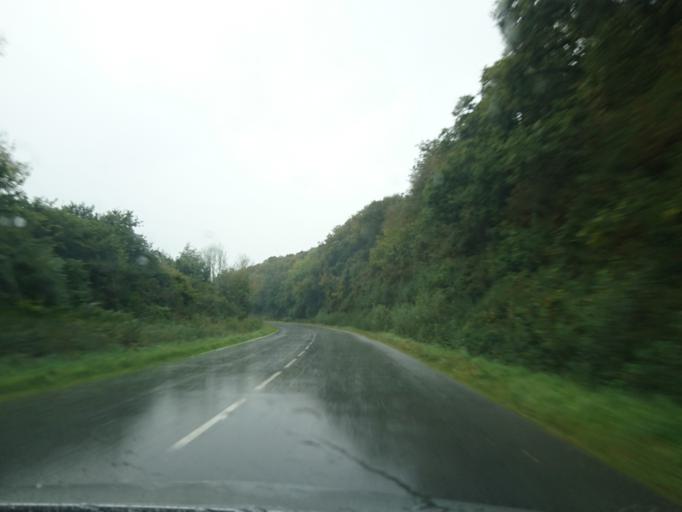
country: FR
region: Brittany
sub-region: Departement du Finistere
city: Plouvien
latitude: 48.5395
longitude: -4.4847
